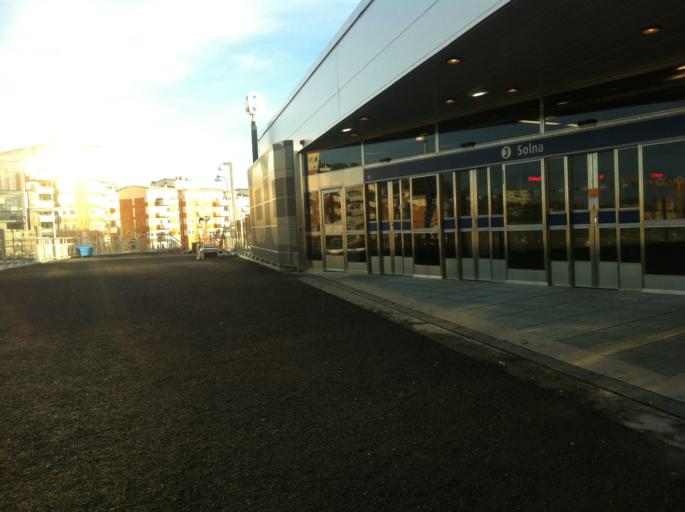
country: SE
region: Stockholm
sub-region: Solna Kommun
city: Solna
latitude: 59.3685
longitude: 18.0084
